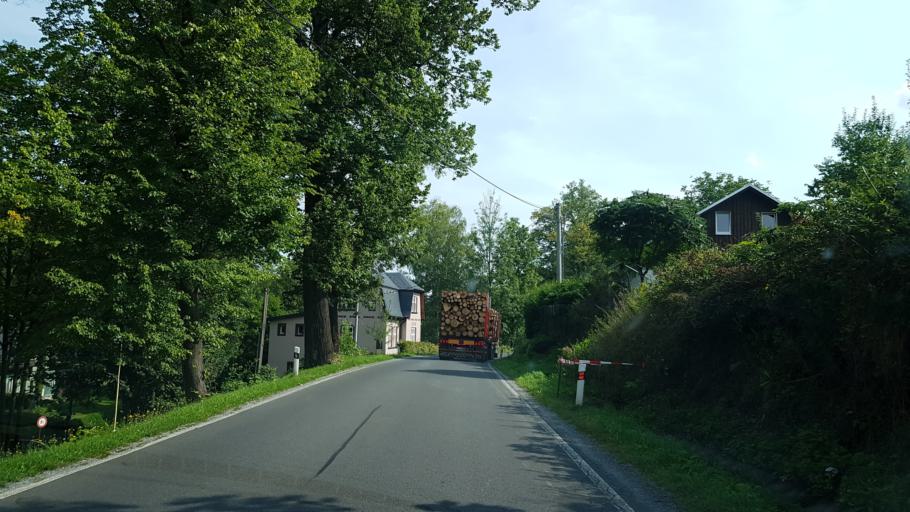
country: CZ
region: Olomoucky
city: Zlate Hory
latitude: 50.2416
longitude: 17.3487
